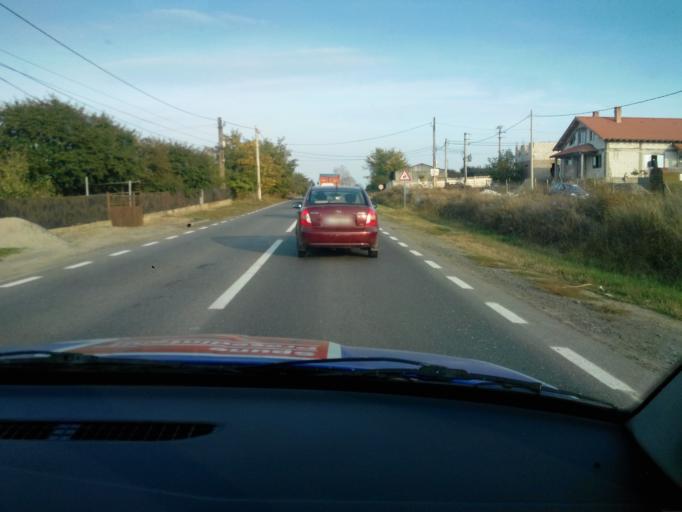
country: RO
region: Tulcea
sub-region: Comuna Somova
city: Mineri
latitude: 45.1671
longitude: 28.7260
